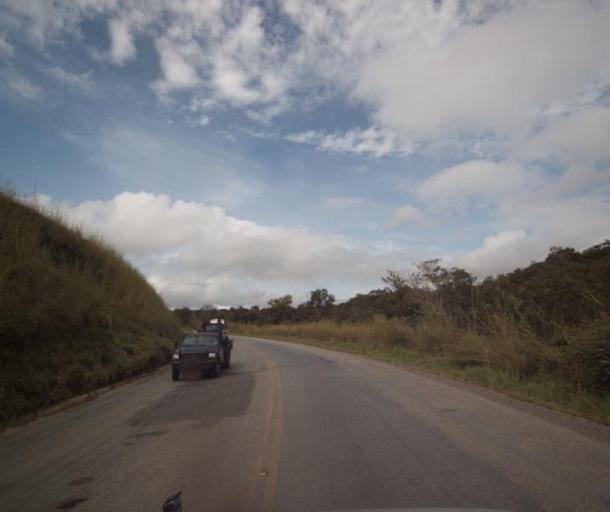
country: BR
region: Goias
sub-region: Pirenopolis
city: Pirenopolis
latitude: -15.7146
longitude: -48.6955
